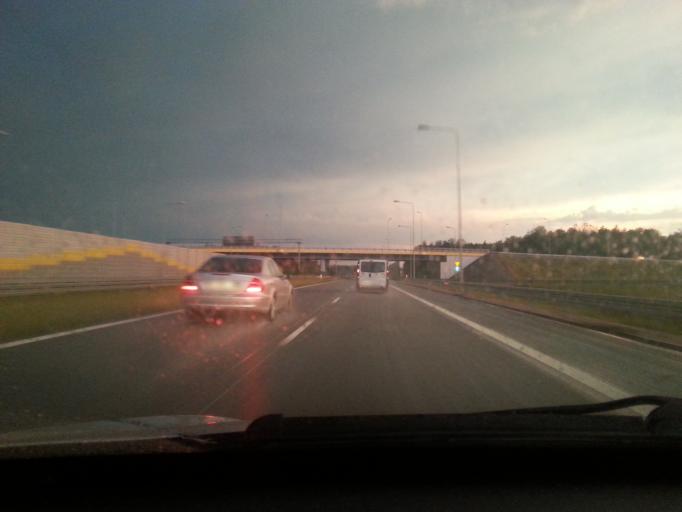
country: PL
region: Lodz Voivodeship
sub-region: Powiat laski
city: Lask
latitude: 51.5753
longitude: 19.1797
